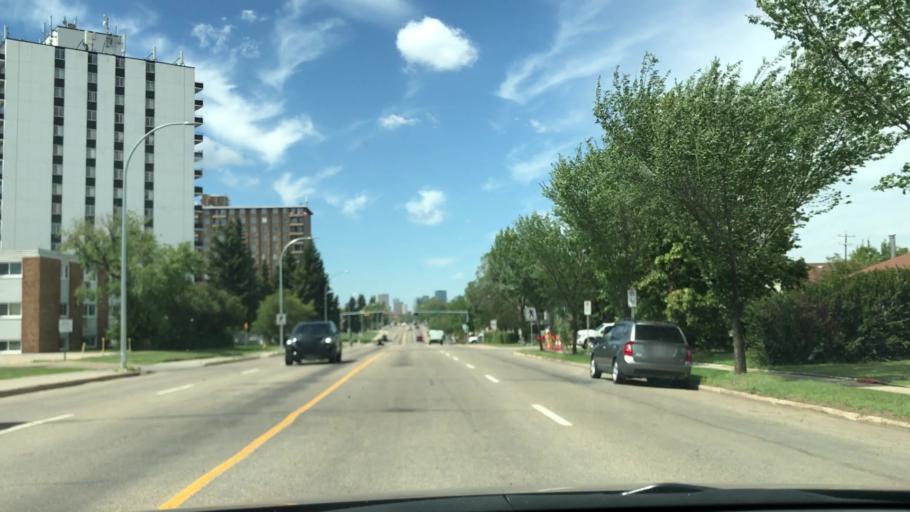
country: CA
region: Alberta
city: Edmonton
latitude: 53.5412
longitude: -113.4270
